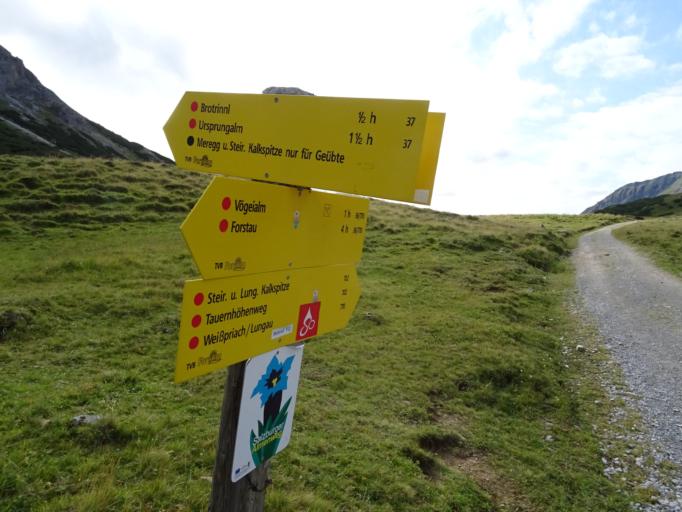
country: AT
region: Salzburg
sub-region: Politischer Bezirk Tamsweg
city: Tweng
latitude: 47.2822
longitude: 13.6007
